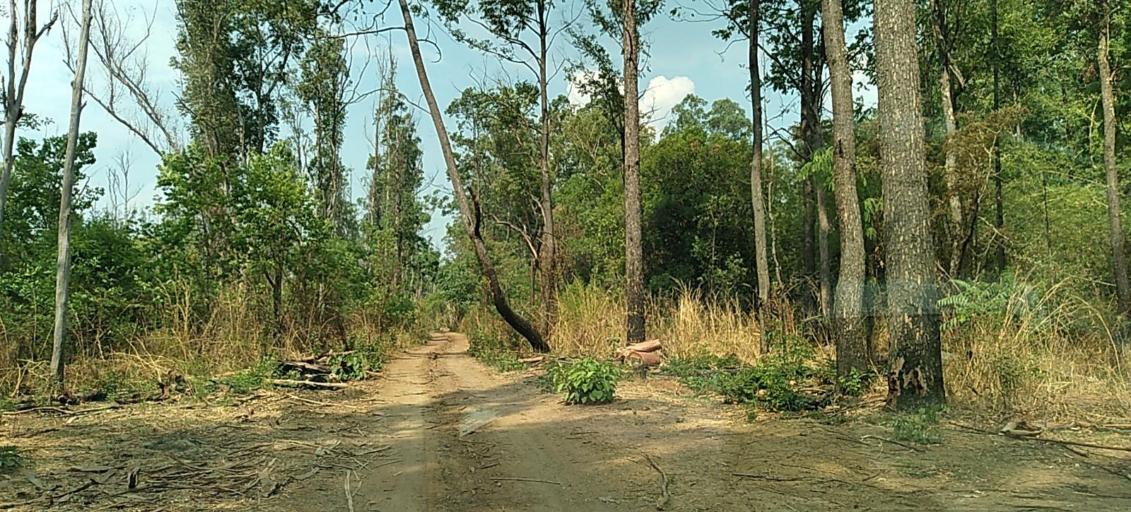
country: ZM
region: Copperbelt
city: Chingola
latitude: -12.7392
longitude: 27.7537
